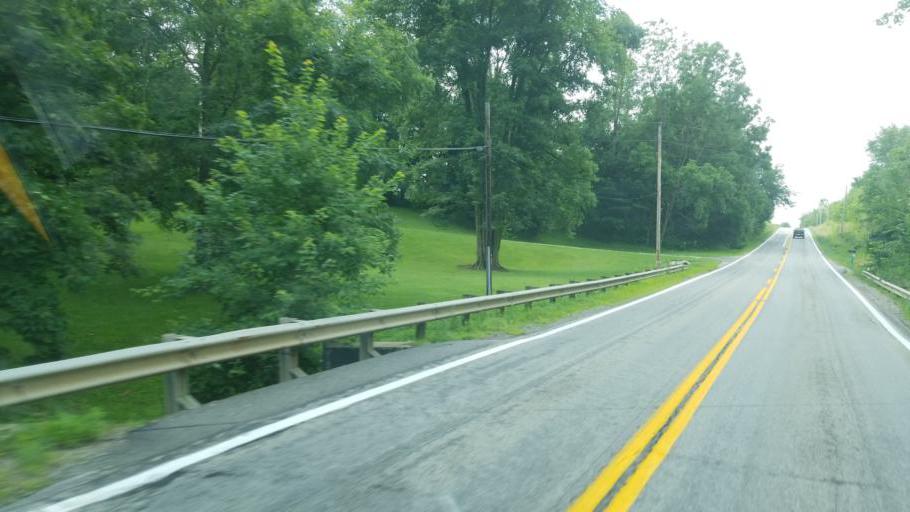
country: US
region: Ohio
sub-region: Knox County
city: Centerburg
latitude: 40.4474
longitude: -82.6974
